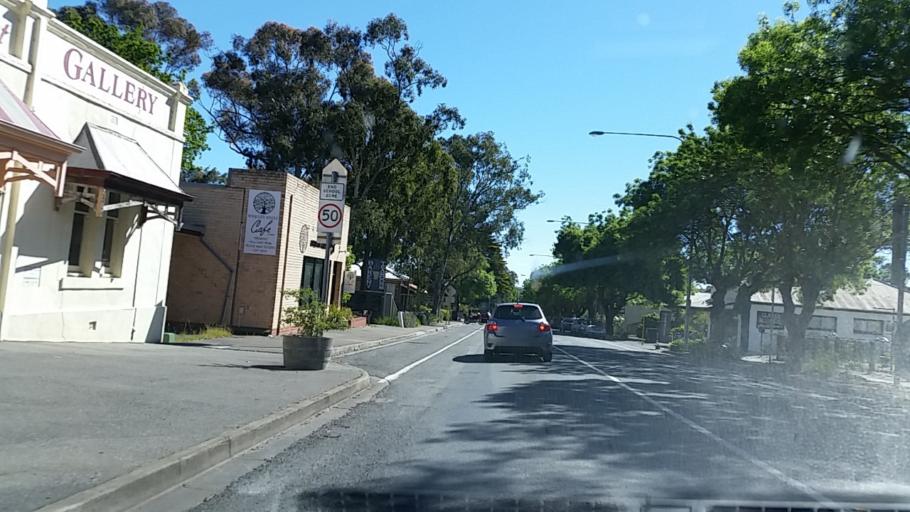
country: AU
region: South Australia
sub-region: Mount Barker
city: Meadows
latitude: -35.1812
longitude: 138.7612
